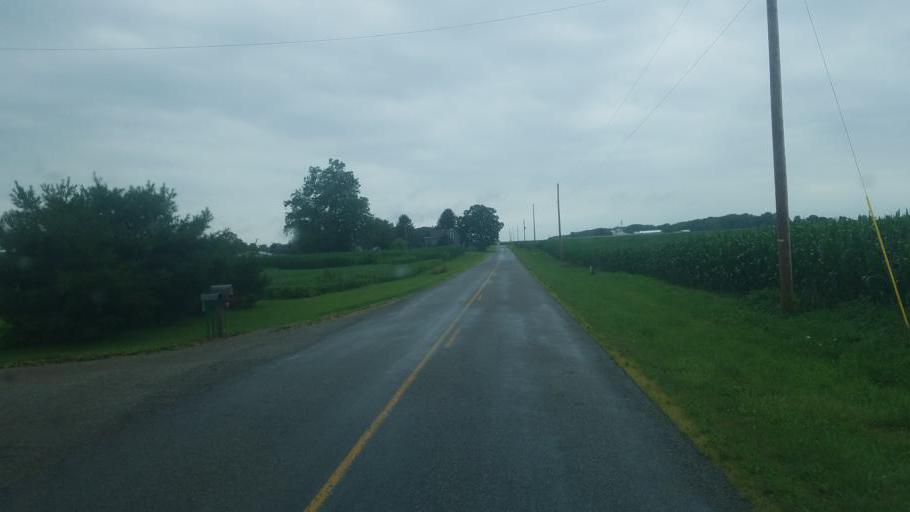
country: US
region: Ohio
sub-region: Hardin County
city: Kenton
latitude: 40.5089
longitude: -83.4935
